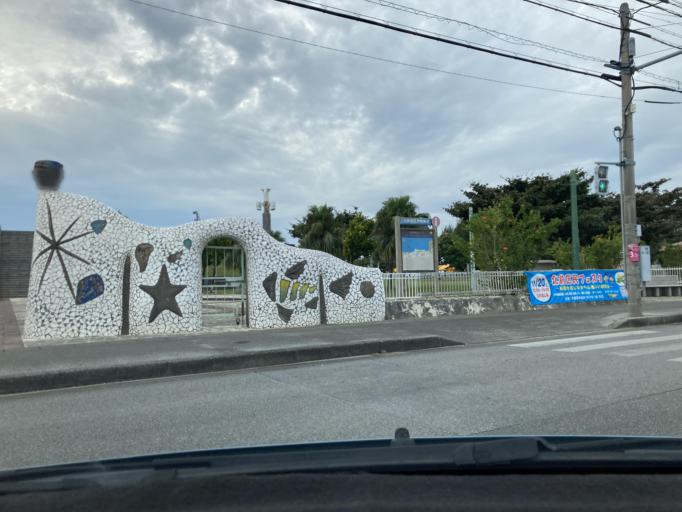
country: JP
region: Okinawa
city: Chatan
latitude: 26.3023
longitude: 127.7593
